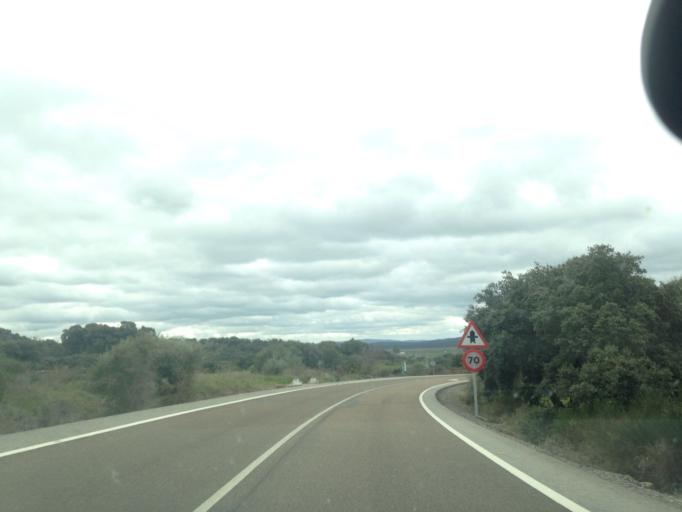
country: ES
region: Extremadura
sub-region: Provincia de Caceres
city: Montanchez
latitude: 39.2164
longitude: -6.1739
